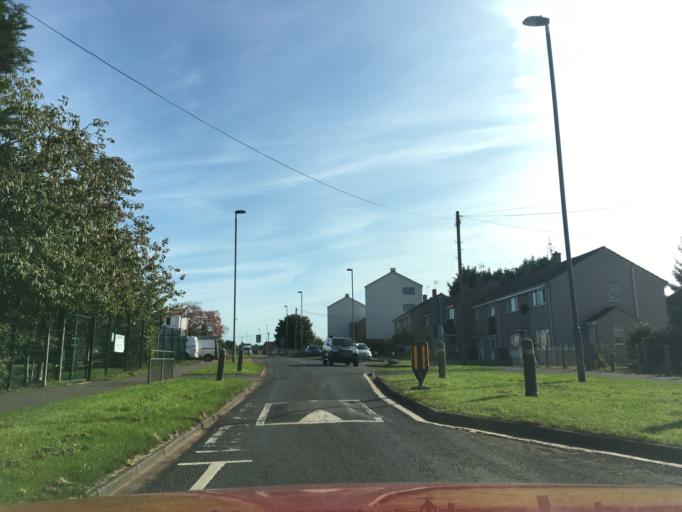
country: GB
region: England
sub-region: South Gloucestershire
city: Yate
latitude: 51.5463
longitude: -2.4249
